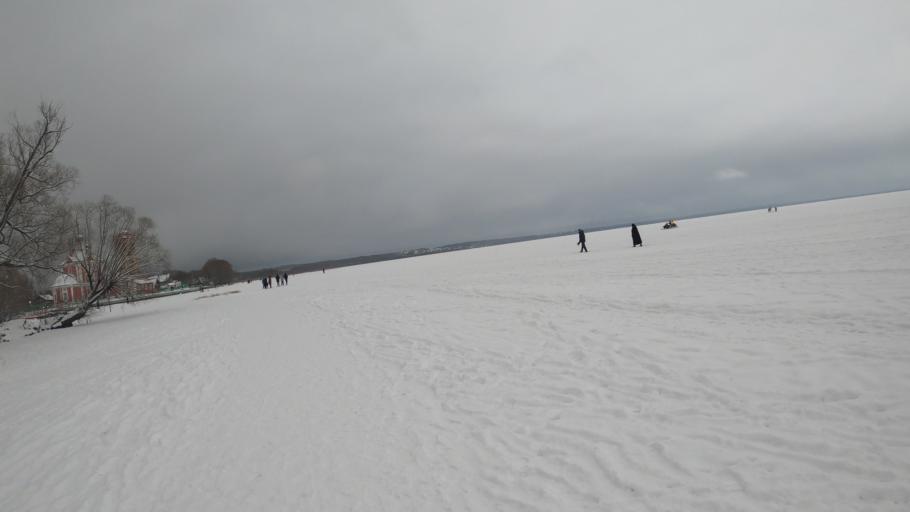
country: RU
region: Jaroslavl
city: Pereslavl'-Zalesskiy
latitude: 56.7367
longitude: 38.8286
